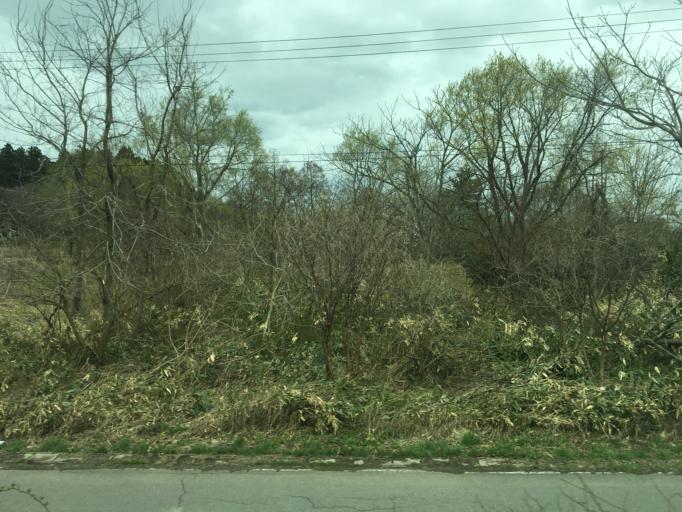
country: JP
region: Aomori
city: Shimokizukuri
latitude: 40.7873
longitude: 140.2965
